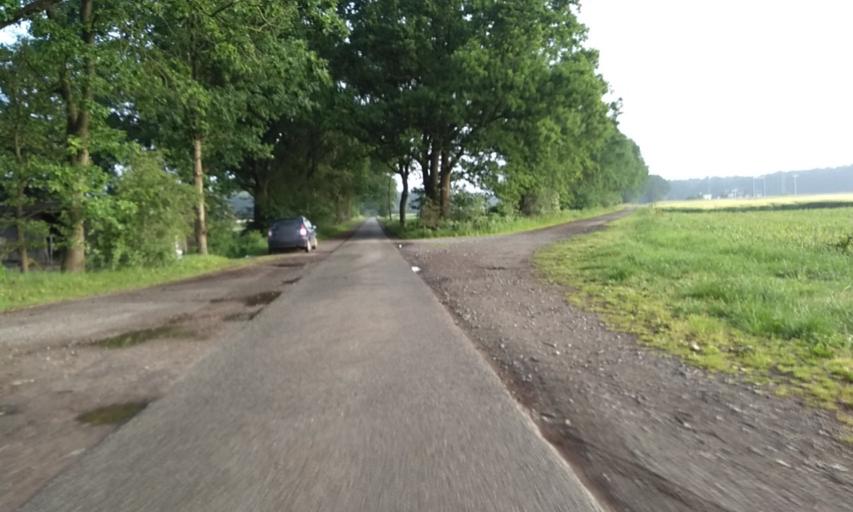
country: DE
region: Lower Saxony
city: Bargstedt
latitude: 53.4907
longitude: 9.4629
